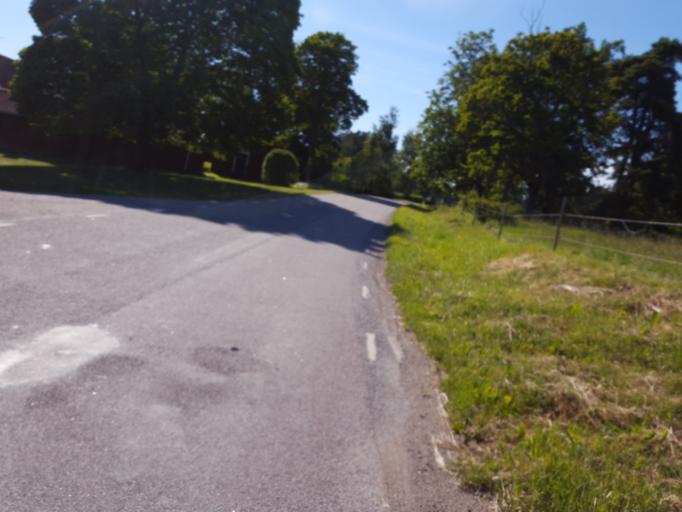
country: SE
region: Uppsala
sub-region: Uppsala Kommun
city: Saevja
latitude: 59.8283
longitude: 17.7636
